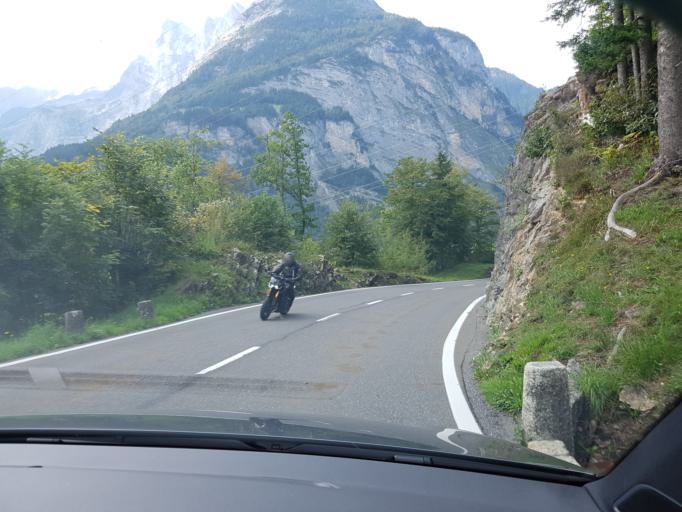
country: CH
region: Bern
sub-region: Interlaken-Oberhasli District
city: Meiringen
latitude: 46.7062
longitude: 8.2352
